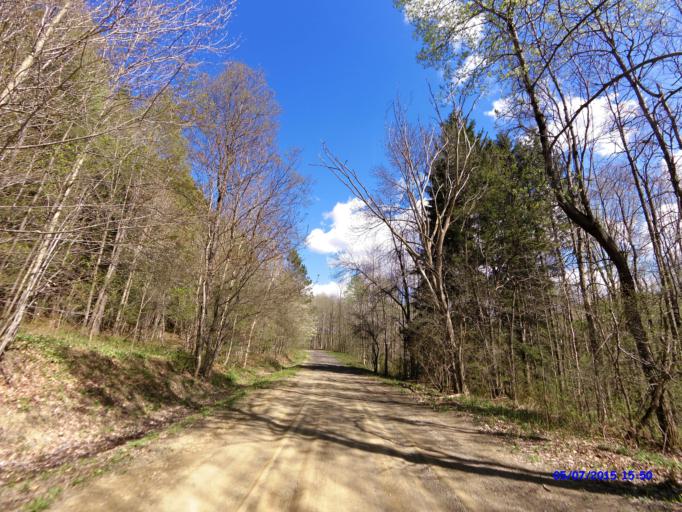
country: US
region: New York
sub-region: Cattaraugus County
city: Franklinville
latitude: 42.3349
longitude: -78.5514
